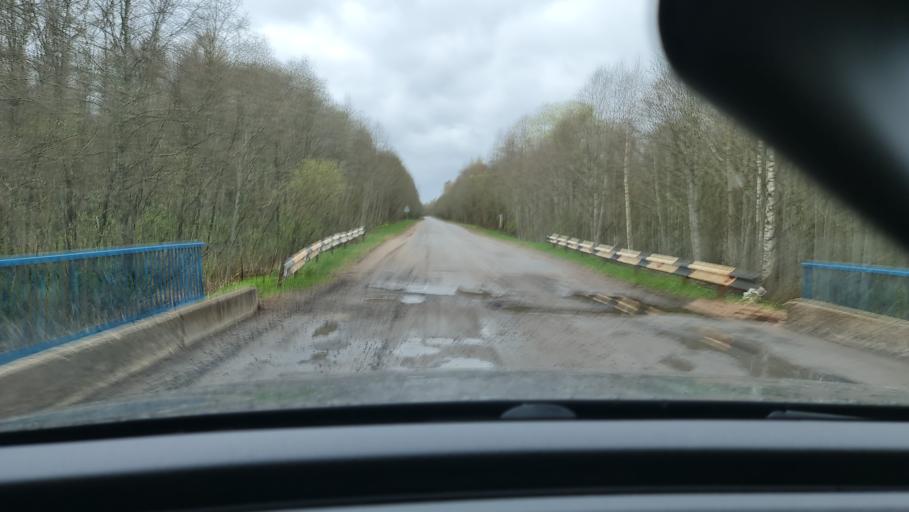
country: RU
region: Novgorod
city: Marevo
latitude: 57.1038
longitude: 31.7623
